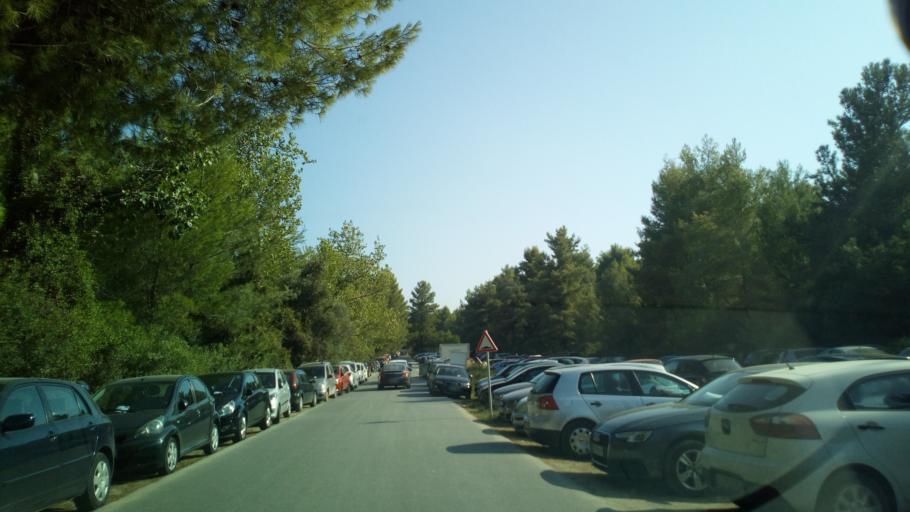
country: GR
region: Central Macedonia
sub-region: Nomos Chalkidikis
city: Pefkochori
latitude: 39.9625
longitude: 23.6749
